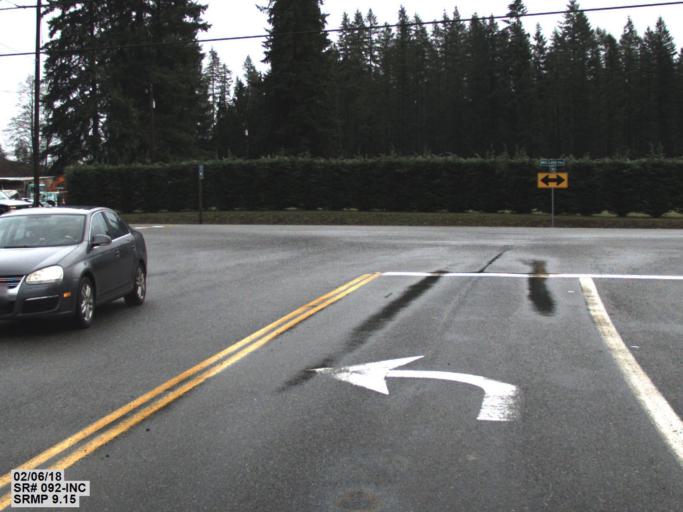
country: US
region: Washington
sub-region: Snohomish County
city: Granite Falls
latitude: 48.0936
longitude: -121.9618
